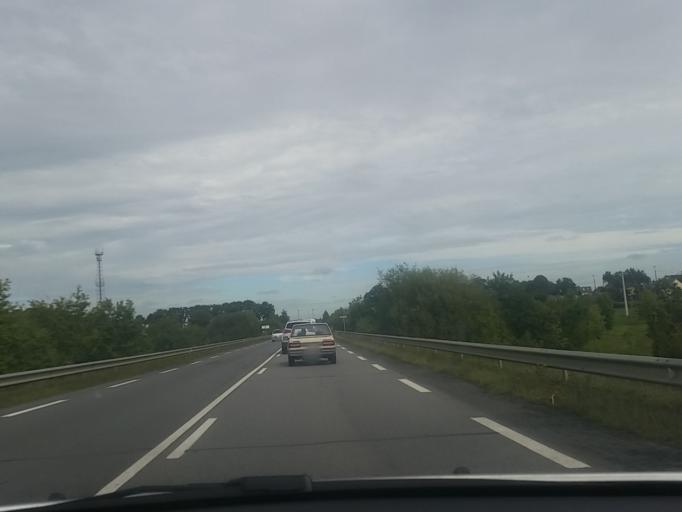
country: FR
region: Brittany
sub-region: Departement d'Ille-et-Vilaine
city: Martigne-Ferchaud
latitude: 47.8241
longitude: -1.3274
